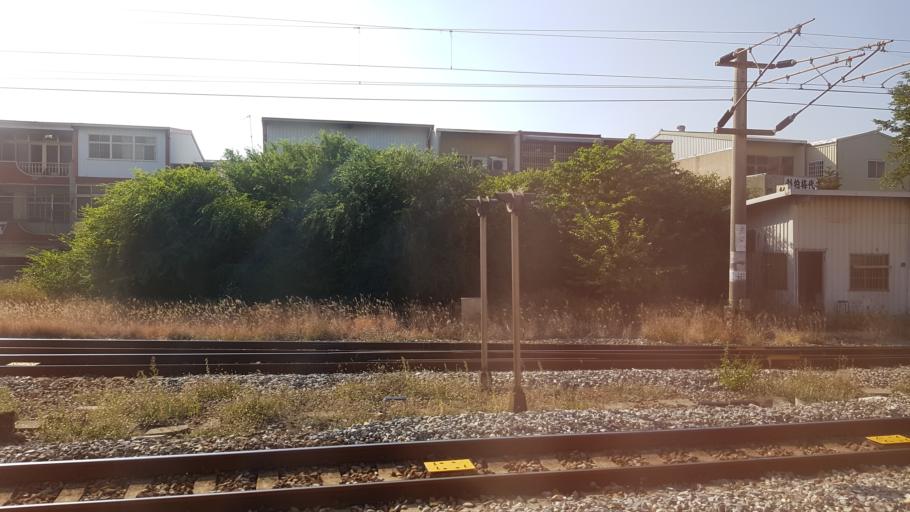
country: TW
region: Taiwan
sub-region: Miaoli
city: Miaoli
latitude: 24.5717
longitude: 120.8218
